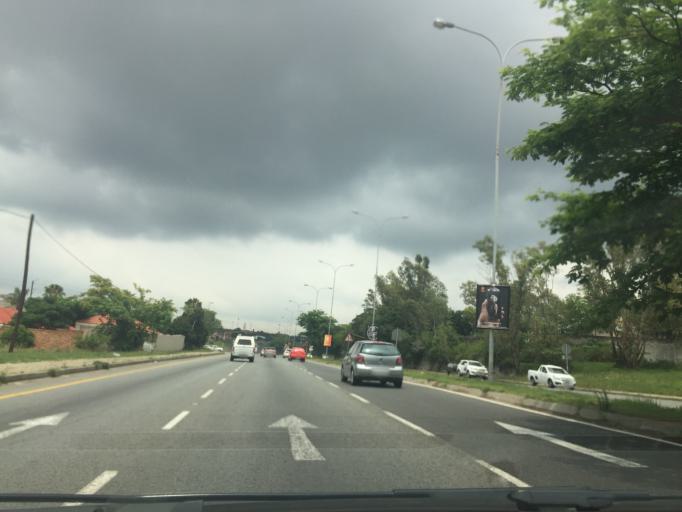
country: ZA
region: Gauteng
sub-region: City of Johannesburg Metropolitan Municipality
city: Modderfontein
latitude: -26.0834
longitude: 28.1046
